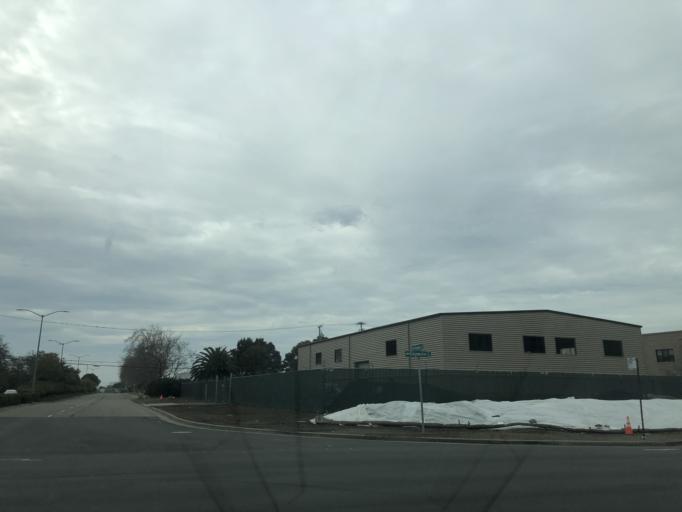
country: US
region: California
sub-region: Alameda County
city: Alameda
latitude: 37.7434
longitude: -122.2044
